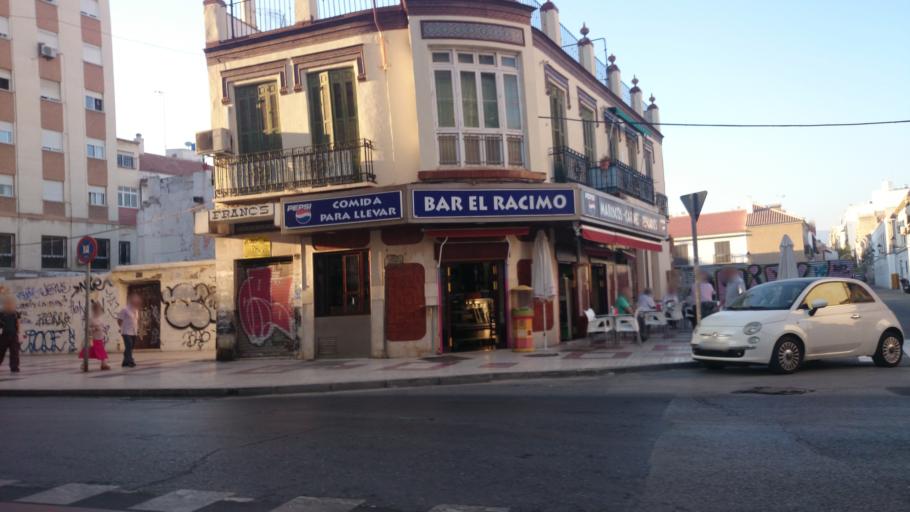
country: ES
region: Andalusia
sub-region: Provincia de Malaga
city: Malaga
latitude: 36.7216
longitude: -4.4300
